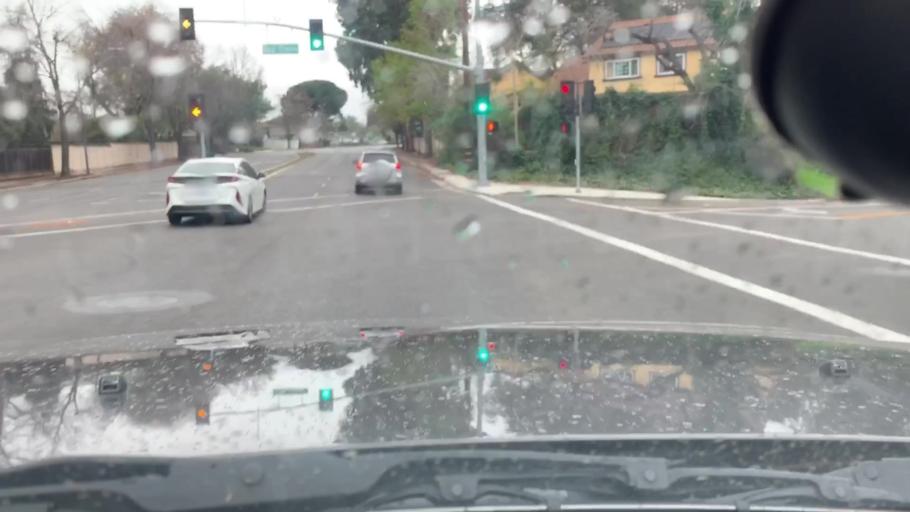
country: US
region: California
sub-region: Santa Clara County
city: Cambrian Park
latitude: 37.2827
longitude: -121.9225
